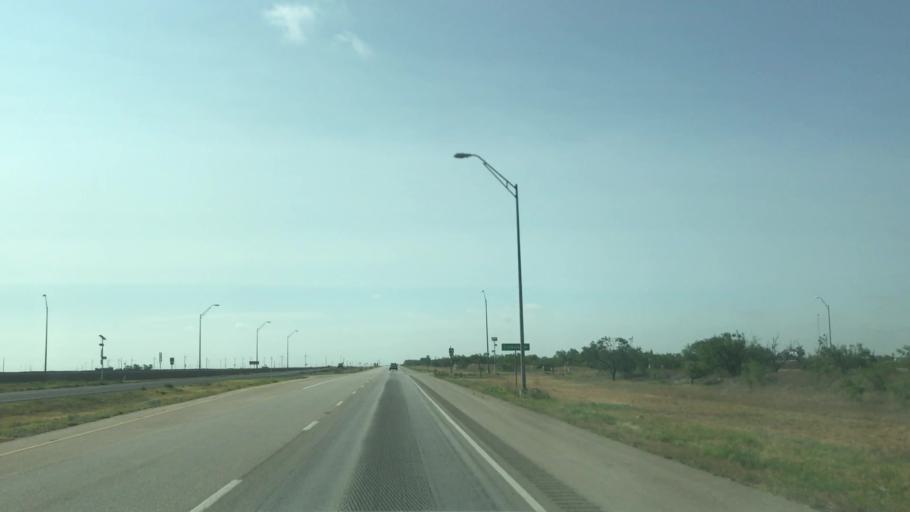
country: US
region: Texas
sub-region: Scurry County
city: Snyder
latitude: 32.6231
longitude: -100.7560
